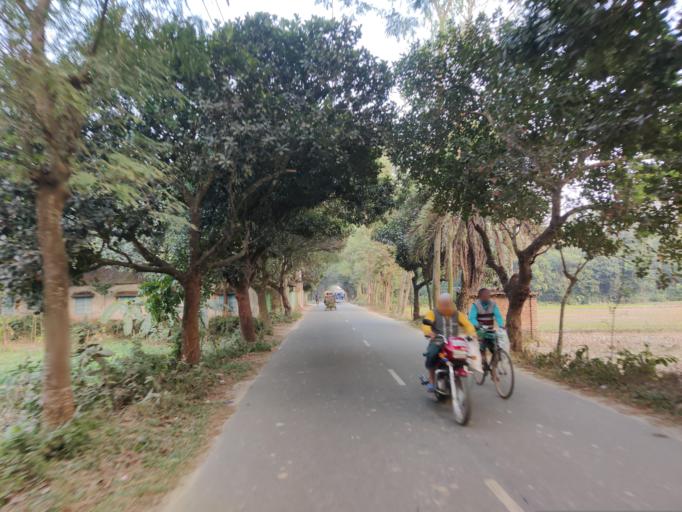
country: BD
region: Dhaka
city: Bajitpur
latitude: 24.1584
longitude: 90.8041
